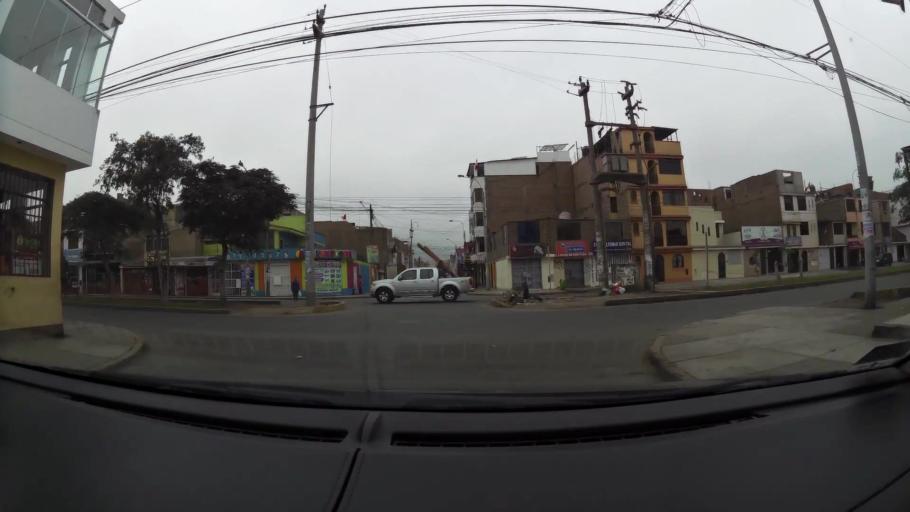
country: PE
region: Lima
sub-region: Lima
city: Independencia
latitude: -11.9601
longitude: -77.0730
